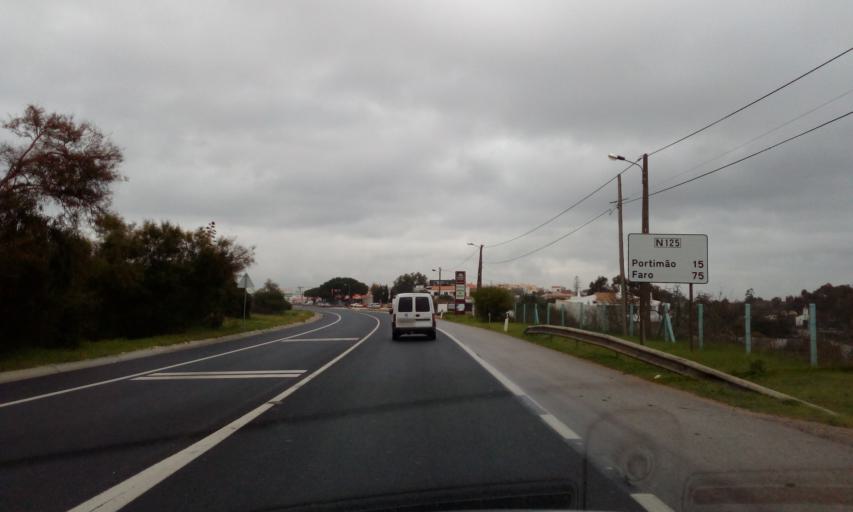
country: PT
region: Faro
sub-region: Lagos
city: Lagos
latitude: 37.1333
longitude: -8.6651
